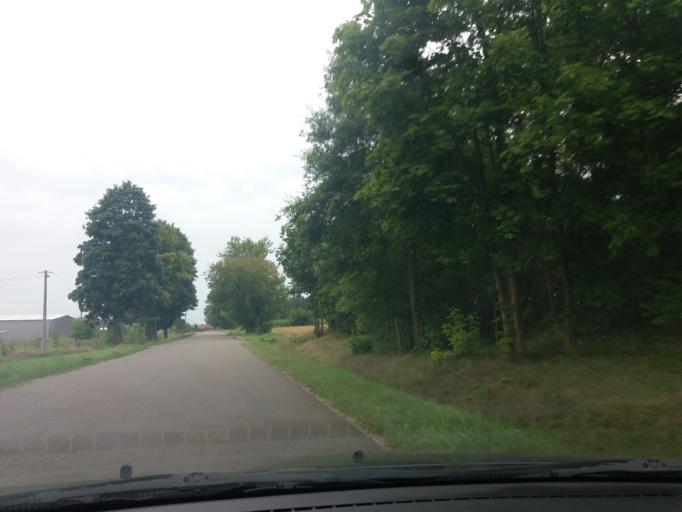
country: PL
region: Masovian Voivodeship
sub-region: Powiat mlawski
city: Wieczfnia Koscielna
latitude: 53.2017
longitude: 20.4911
